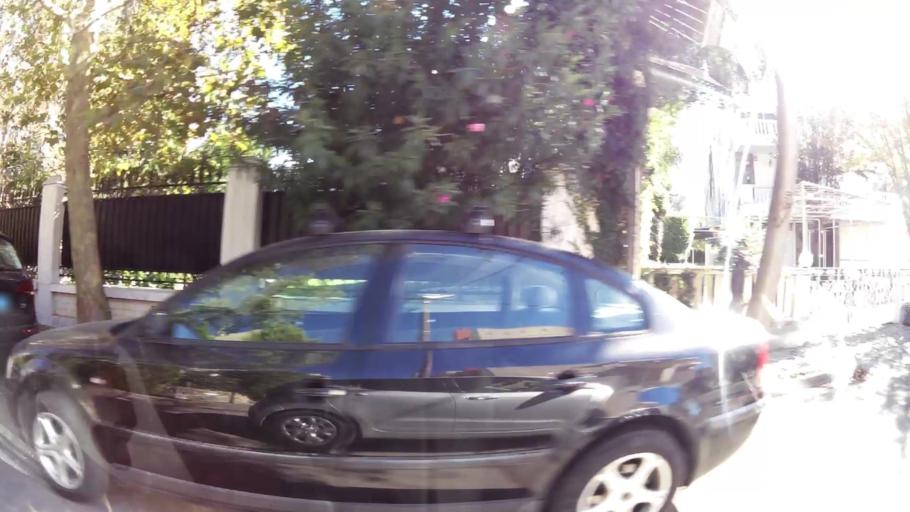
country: GR
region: Attica
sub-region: Nomarchia Athinas
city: Kifisia
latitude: 38.0829
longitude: 23.8022
